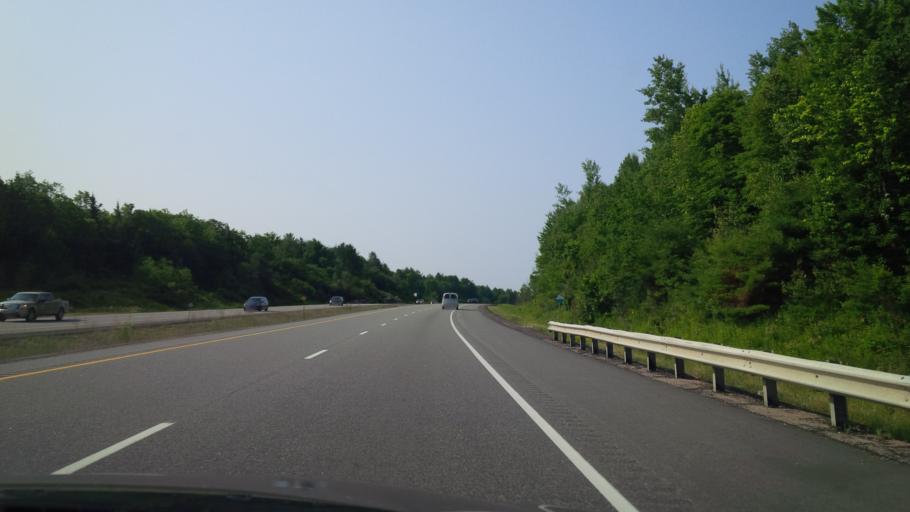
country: CA
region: Ontario
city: Bracebridge
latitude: 45.0276
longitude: -79.2923
